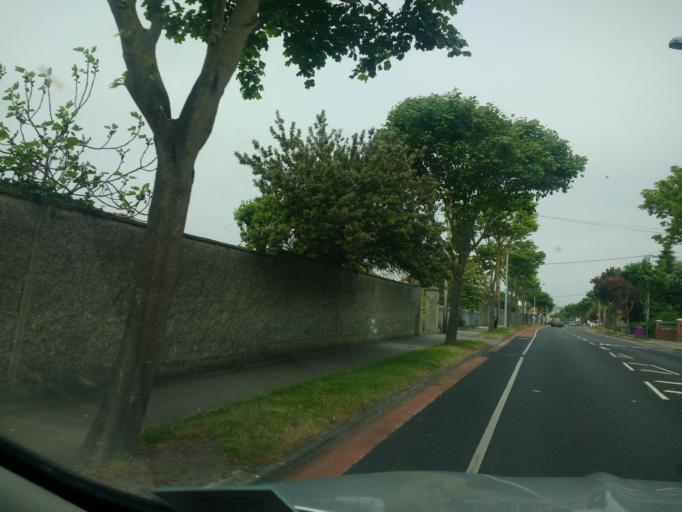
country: IE
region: Leinster
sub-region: Fingal County
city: Baldoyle
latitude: 53.3951
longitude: -6.1260
